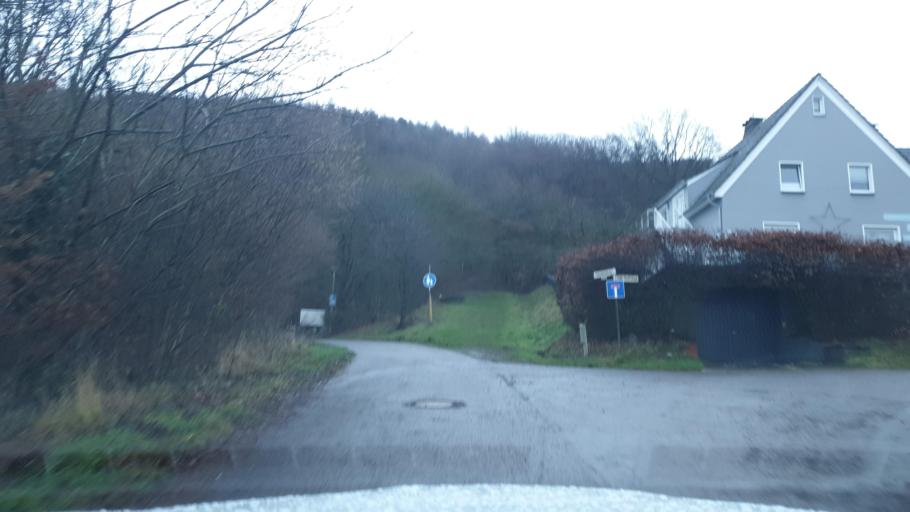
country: DE
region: North Rhine-Westphalia
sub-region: Regierungsbezirk Detmold
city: Hille
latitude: 52.2682
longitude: 8.7616
